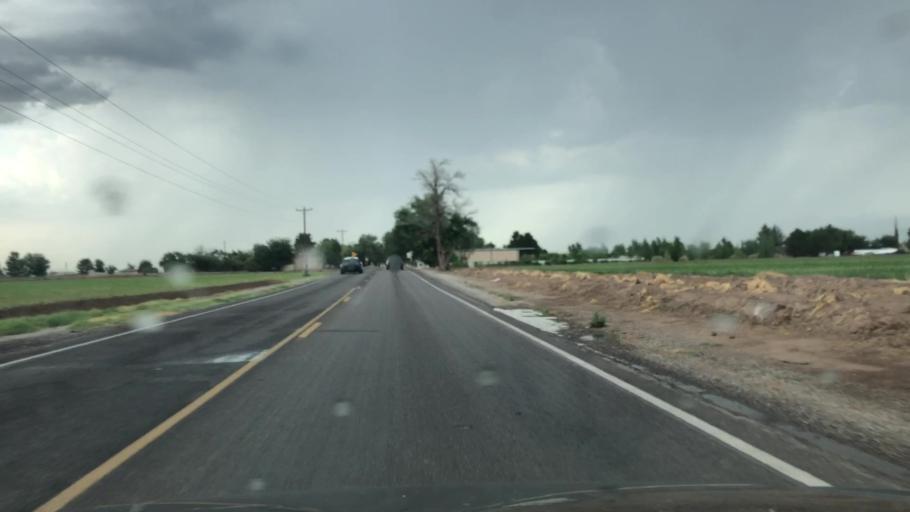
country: US
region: New Mexico
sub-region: Dona Ana County
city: Berino
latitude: 32.0470
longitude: -106.6748
